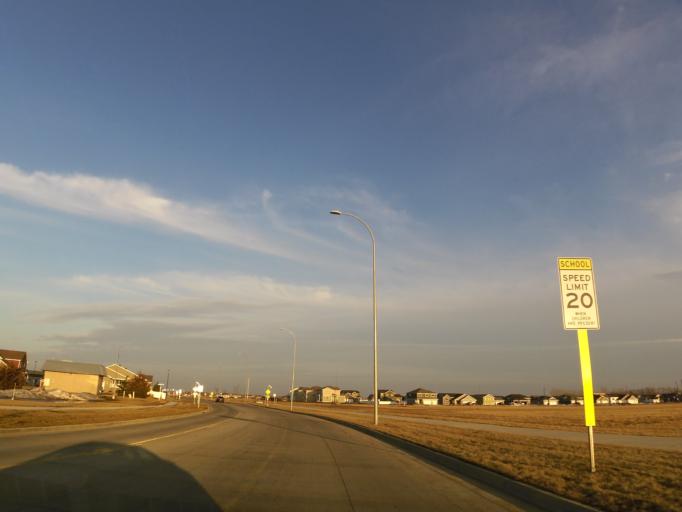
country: US
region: North Dakota
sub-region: Grand Forks County
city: Grand Forks
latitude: 47.8823
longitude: -97.0764
